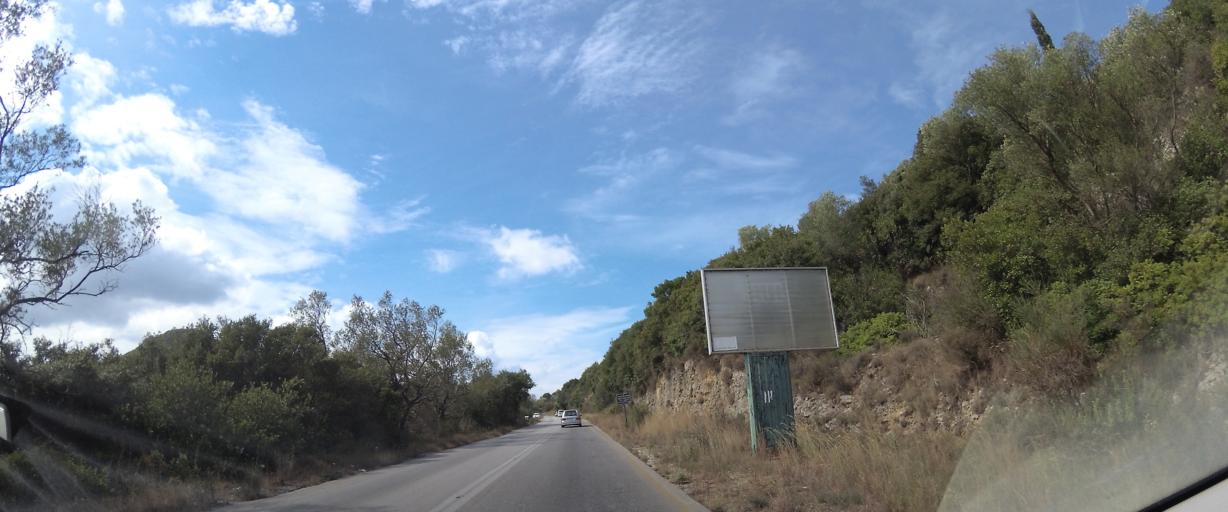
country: GR
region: Ionian Islands
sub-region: Nomos Kerkyras
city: Agios Georgis
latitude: 39.7062
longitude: 19.7516
